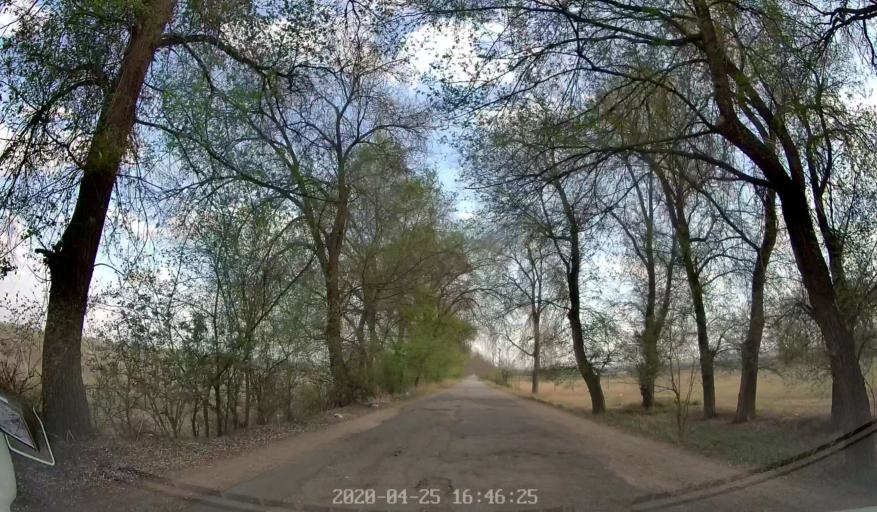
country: MD
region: Chisinau
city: Vadul lui Voda
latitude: 47.1411
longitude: 29.0682
